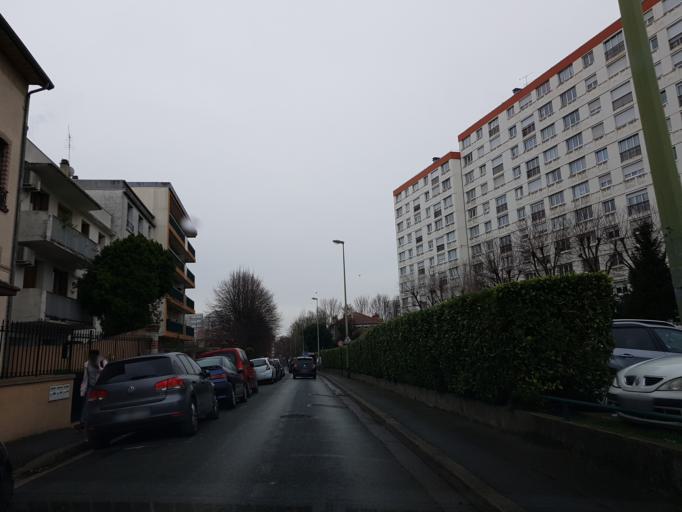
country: FR
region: Ile-de-France
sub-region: Departement du Val-de-Marne
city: Vitry-sur-Seine
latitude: 48.7950
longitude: 2.3904
